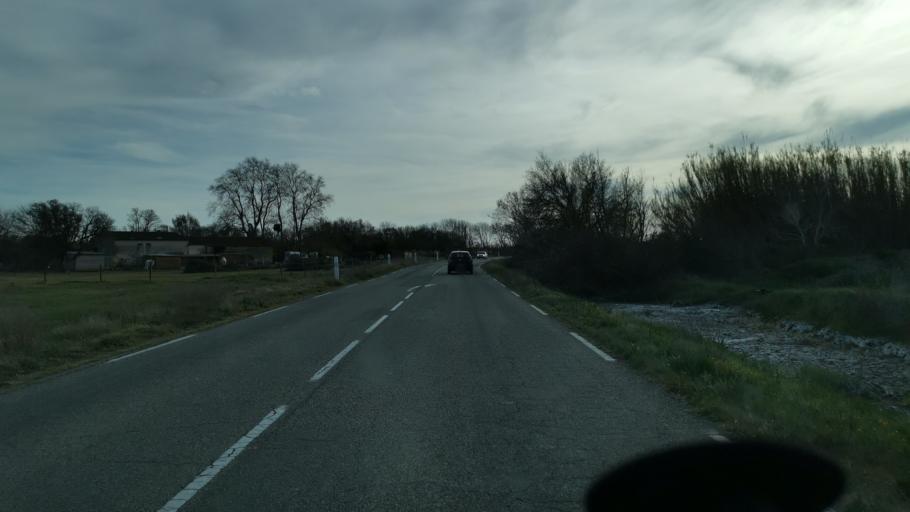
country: FR
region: Provence-Alpes-Cote d'Azur
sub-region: Departement des Bouches-du-Rhone
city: Saint-Martin-de-Crau
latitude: 43.5649
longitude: 4.7404
